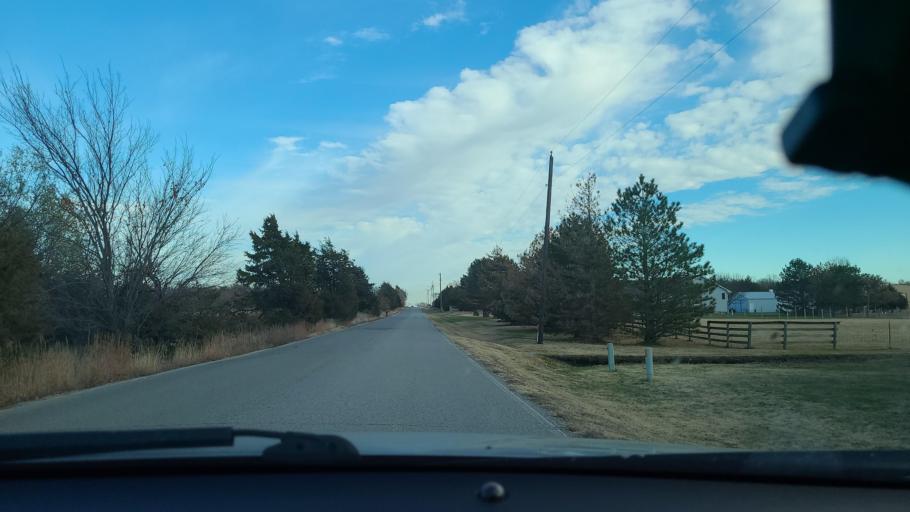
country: US
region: Kansas
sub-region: Sedgwick County
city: Goddard
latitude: 37.6496
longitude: -97.5861
